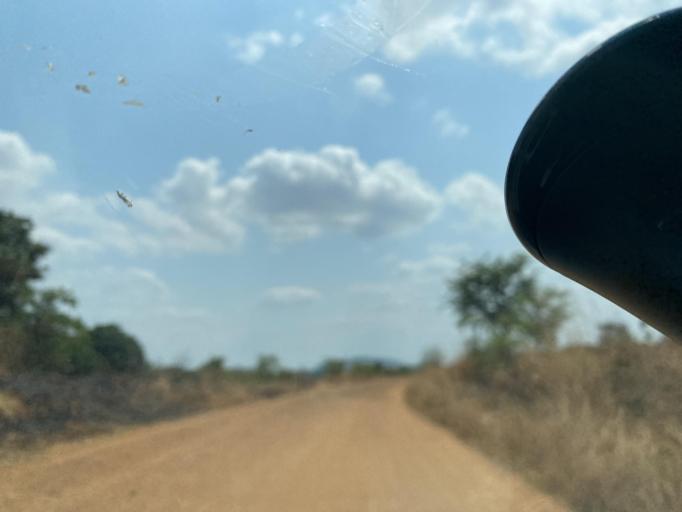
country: ZM
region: Lusaka
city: Chongwe
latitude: -15.5922
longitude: 28.7956
